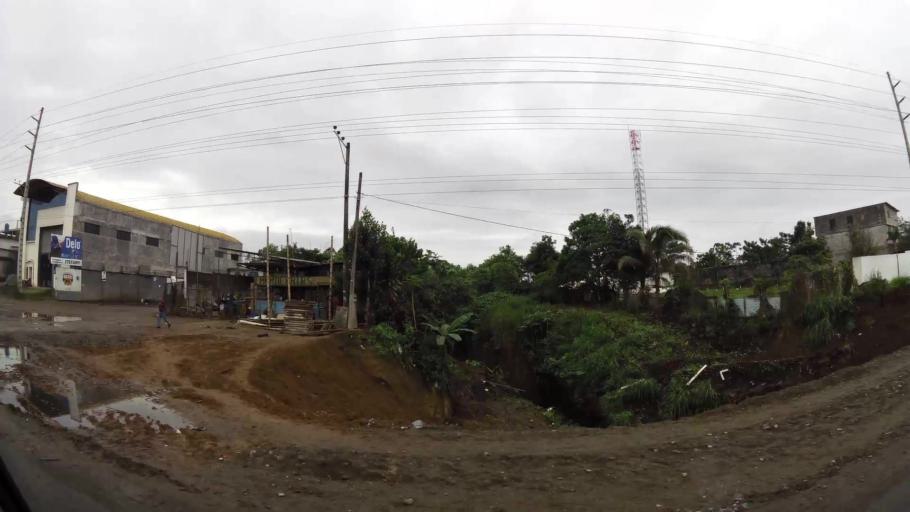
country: EC
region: Santo Domingo de los Tsachilas
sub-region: Canton Santo Domingo de los Colorados
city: Santo Domingo de los Colorados
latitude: -0.2619
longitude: -79.2026
